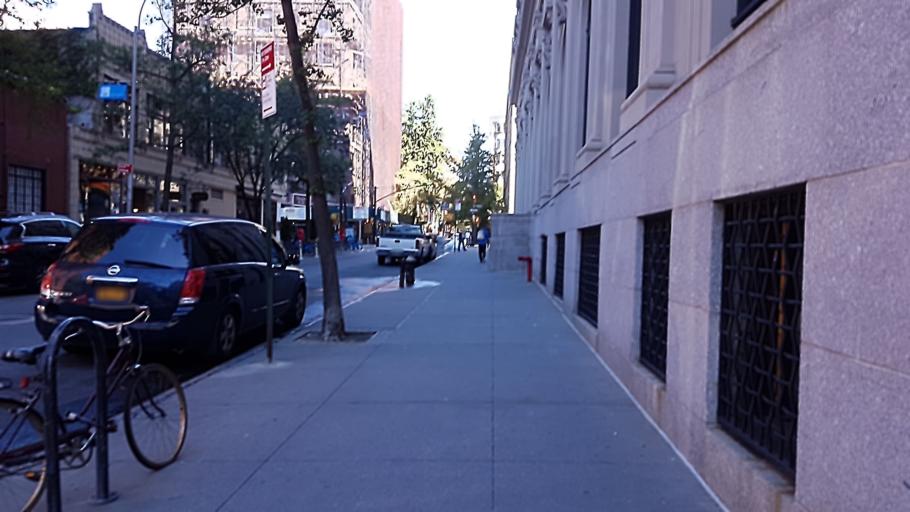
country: US
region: New York
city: New York City
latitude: 40.6946
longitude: -73.9960
